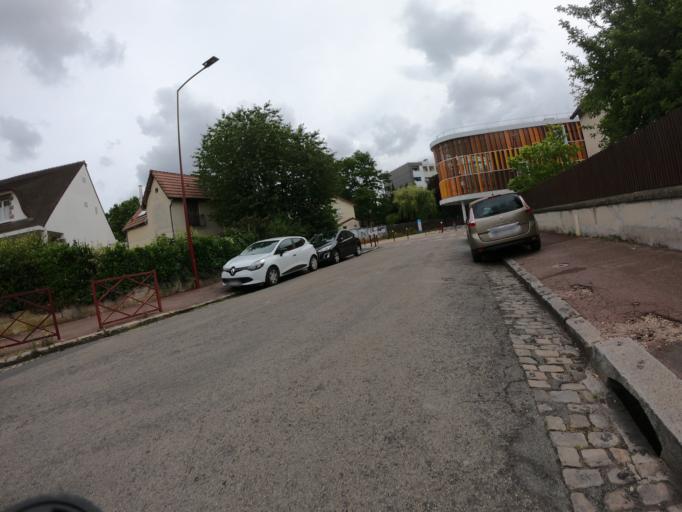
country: FR
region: Ile-de-France
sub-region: Departement du Val-de-Marne
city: Fresnes
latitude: 48.7580
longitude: 2.3201
